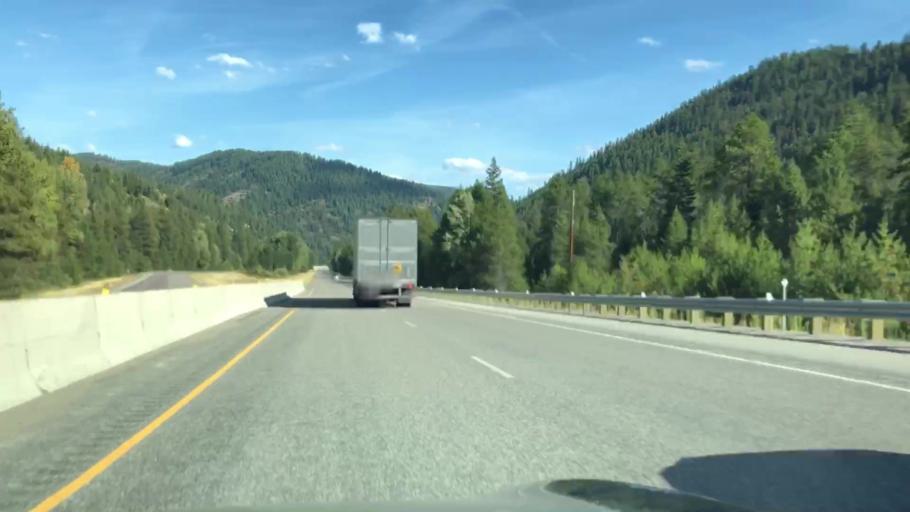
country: US
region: Montana
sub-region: Sanders County
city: Thompson Falls
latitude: 47.3598
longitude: -115.3165
